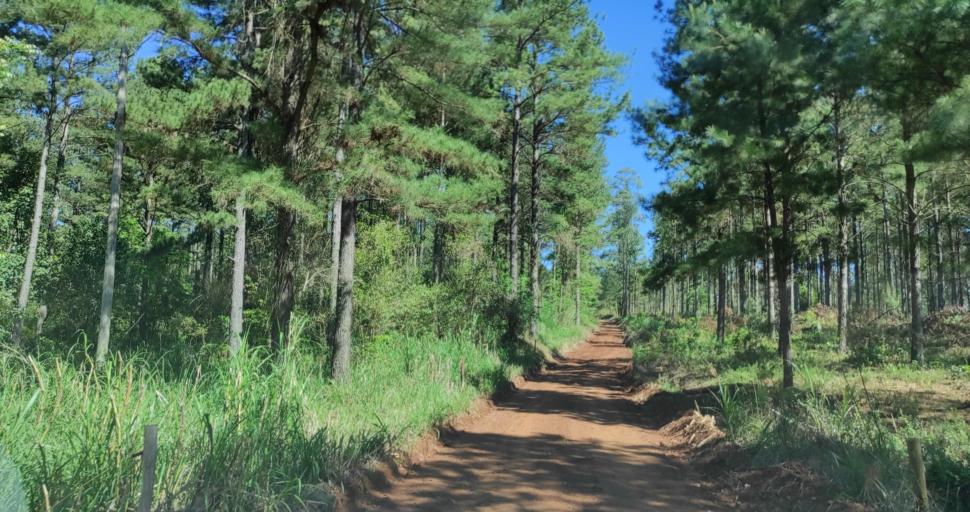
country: AR
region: Misiones
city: Ruiz de Montoya
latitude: -26.9451
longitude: -54.9803
